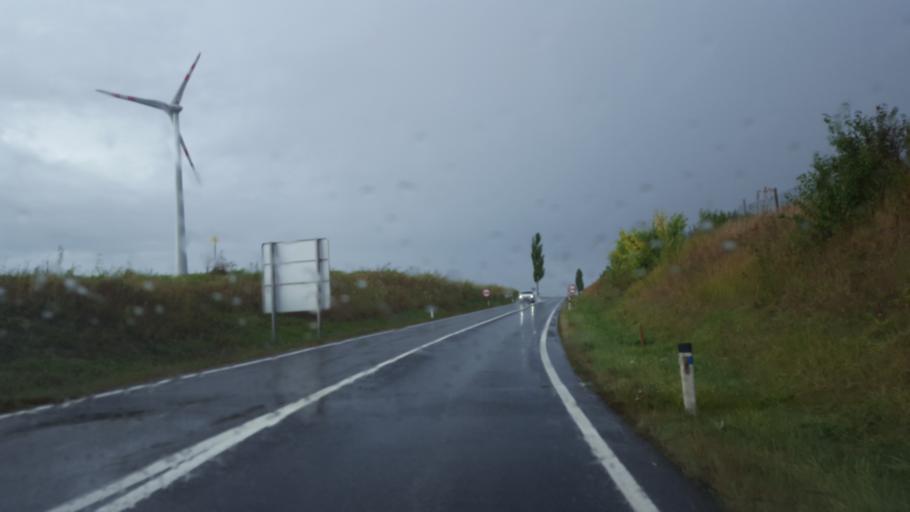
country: AT
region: Lower Austria
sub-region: Politischer Bezirk Bruck an der Leitha
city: Bruck an der Leitha
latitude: 48.0268
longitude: 16.7408
